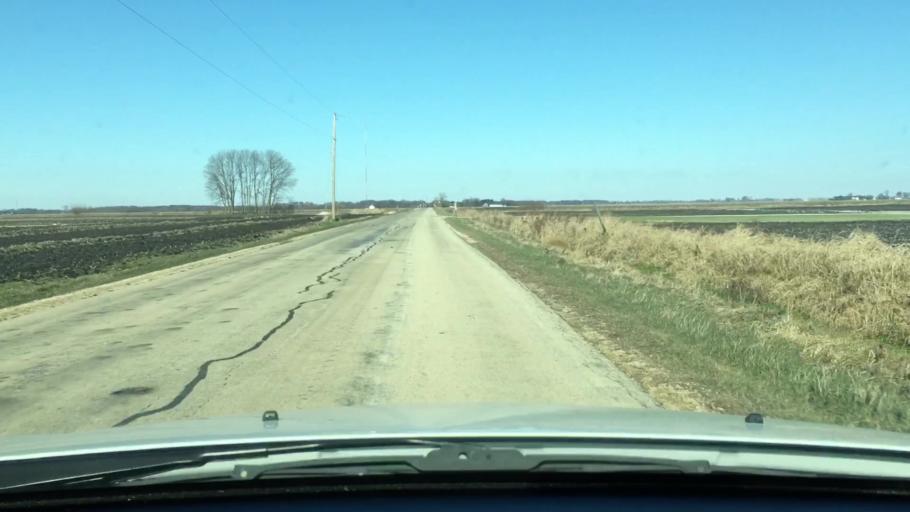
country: US
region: Illinois
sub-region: Ogle County
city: Hillcrest
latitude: 42.0017
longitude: -89.0006
